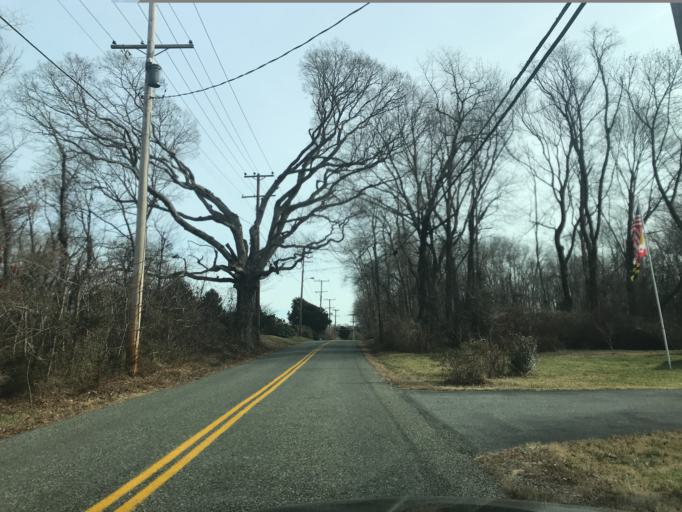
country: US
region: Maryland
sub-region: Harford County
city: Aberdeen
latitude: 39.5741
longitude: -76.1532
